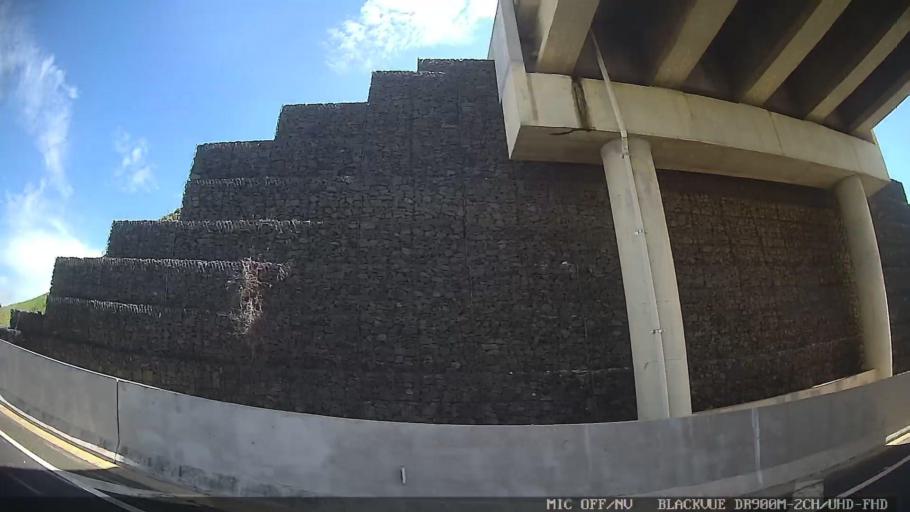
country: BR
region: Sao Paulo
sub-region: Tiete
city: Tiete
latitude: -23.1579
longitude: -47.6548
